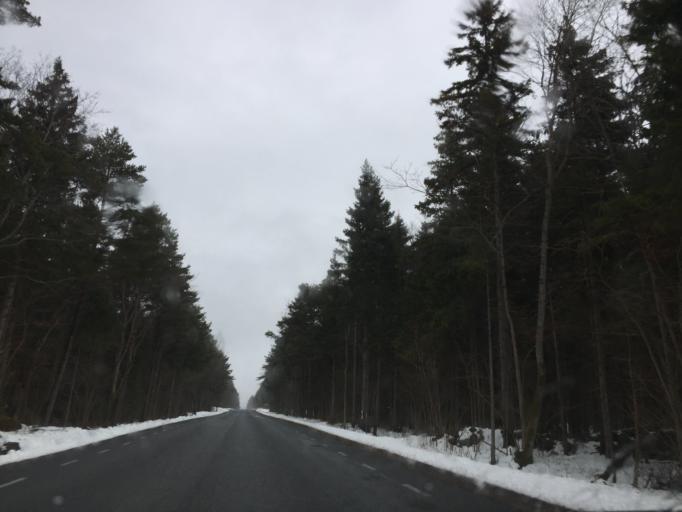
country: EE
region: Saare
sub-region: Kuressaare linn
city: Kuressaare
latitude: 58.3337
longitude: 22.0266
